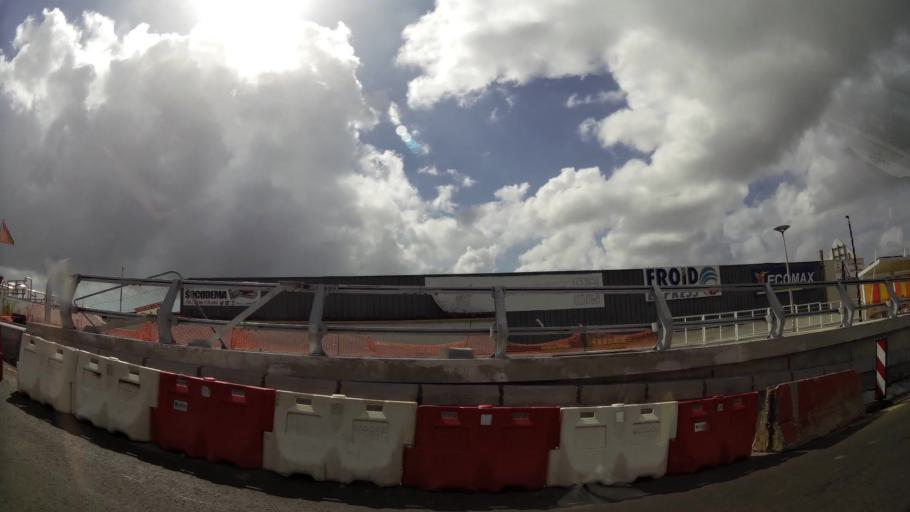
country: MQ
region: Martinique
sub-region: Martinique
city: Le Lamentin
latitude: 14.6094
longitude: -61.0060
